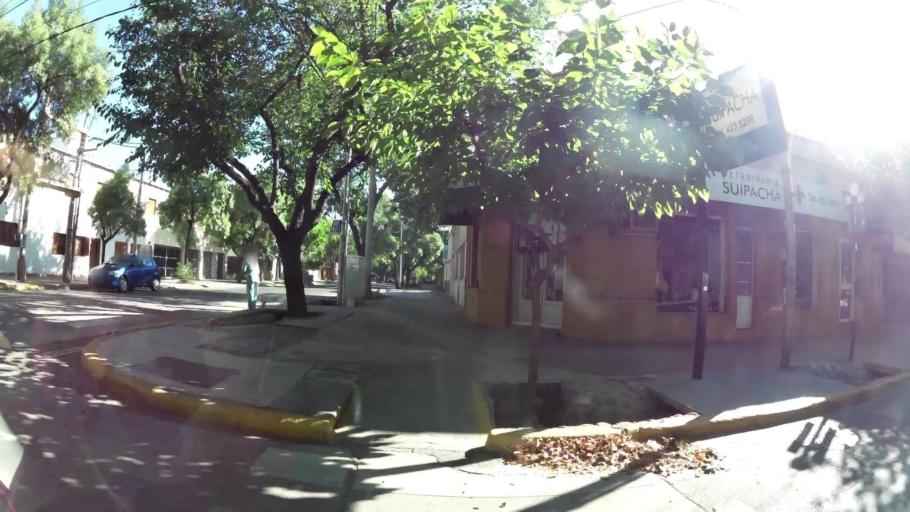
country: AR
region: Mendoza
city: Mendoza
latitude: -32.8778
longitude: -68.8529
